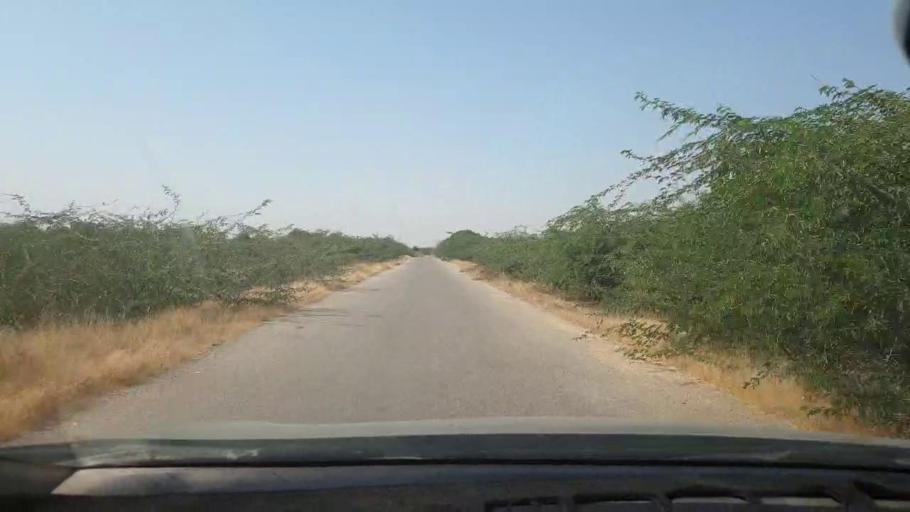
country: PK
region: Sindh
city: Malir Cantonment
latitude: 25.1621
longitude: 67.1586
